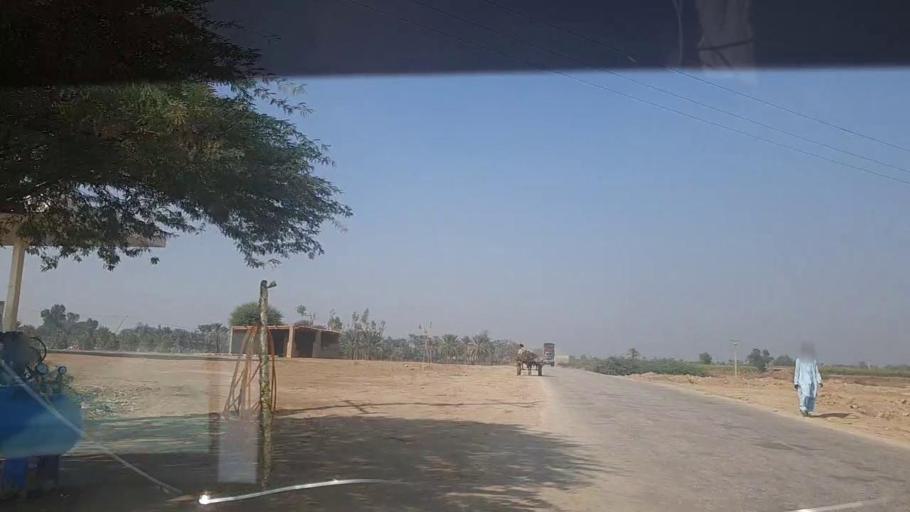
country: PK
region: Sindh
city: Kot Diji
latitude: 27.4156
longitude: 68.6645
